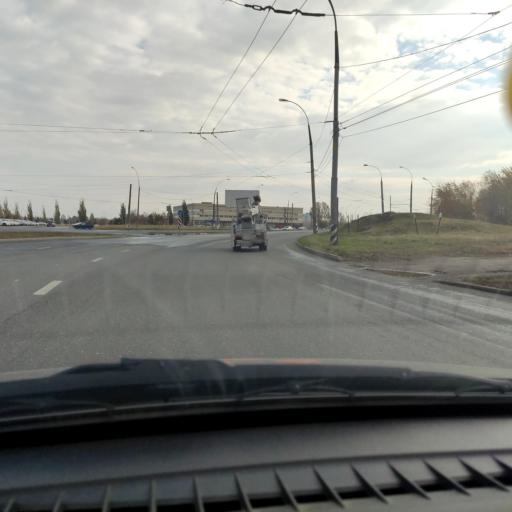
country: RU
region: Samara
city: Tol'yatti
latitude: 53.5556
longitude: 49.2575
